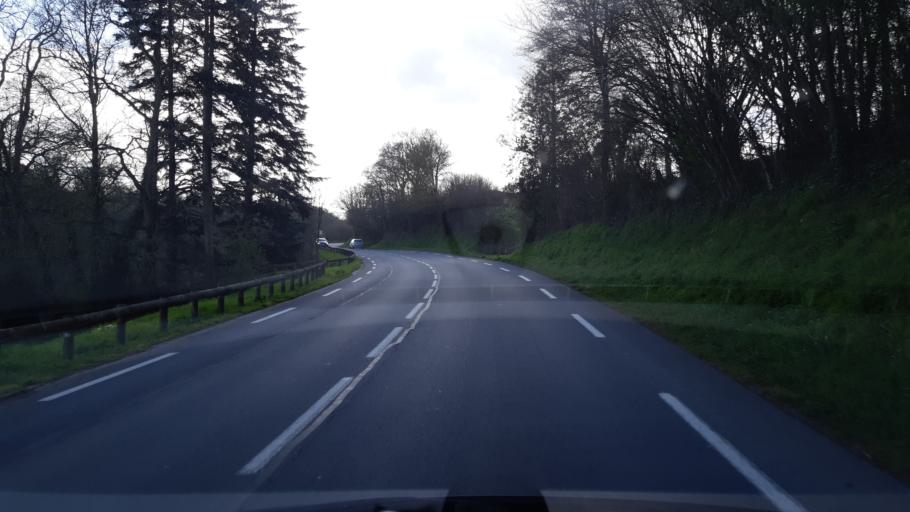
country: FR
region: Lower Normandy
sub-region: Departement de la Manche
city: Agneaux
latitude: 49.0806
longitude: -1.1199
